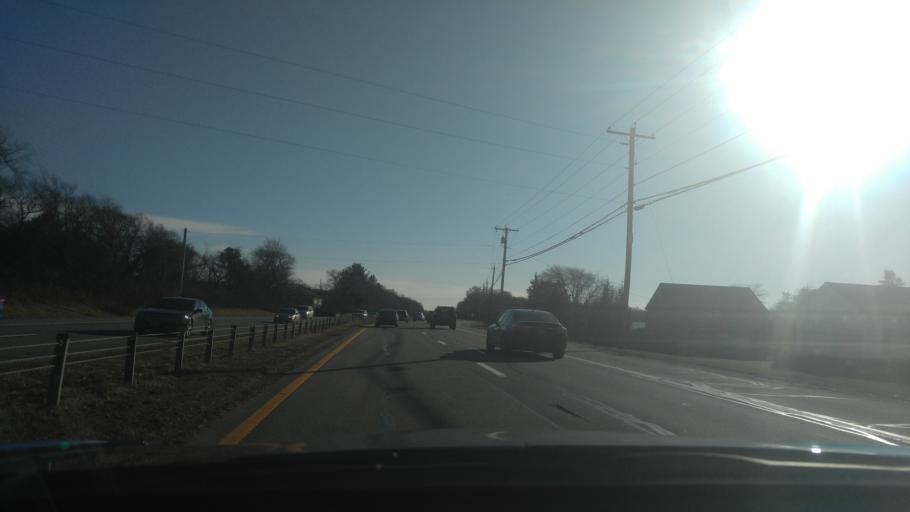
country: US
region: Rhode Island
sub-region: Washington County
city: Narragansett Pier
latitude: 41.4657
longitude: -71.4638
